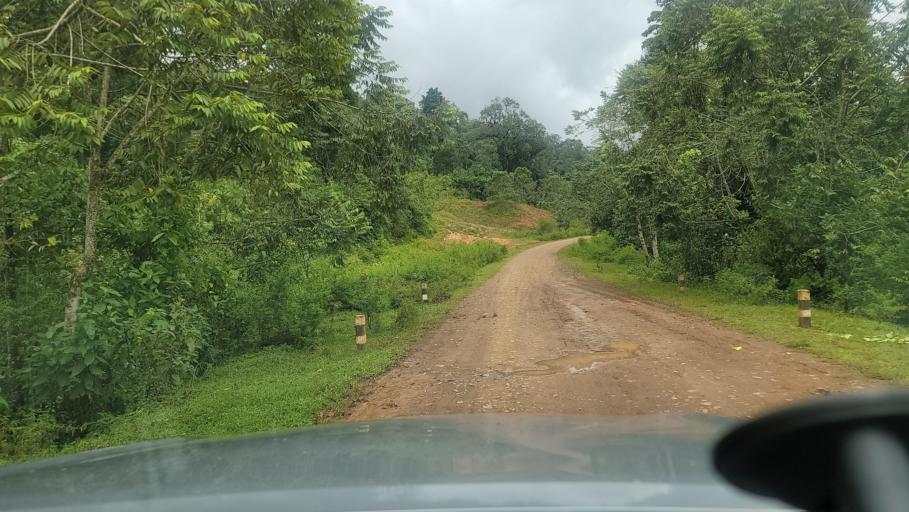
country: ET
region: Southern Nations, Nationalities, and People's Region
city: Bonga
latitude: 7.6386
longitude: 36.2282
